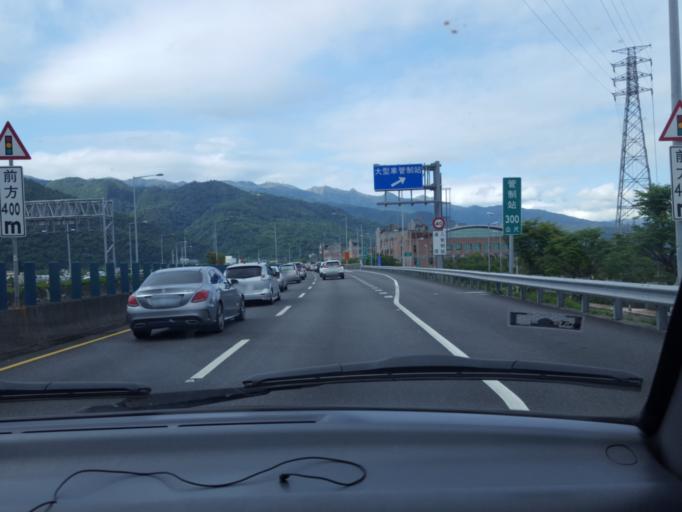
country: TW
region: Taiwan
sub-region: Yilan
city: Yilan
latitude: 24.8307
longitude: 121.7908
